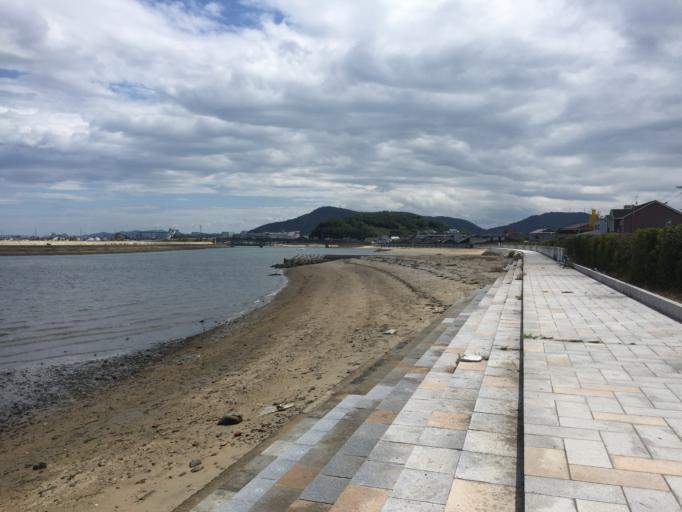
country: JP
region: Kagawa
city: Takamatsu-shi
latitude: 34.3588
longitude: 133.9905
